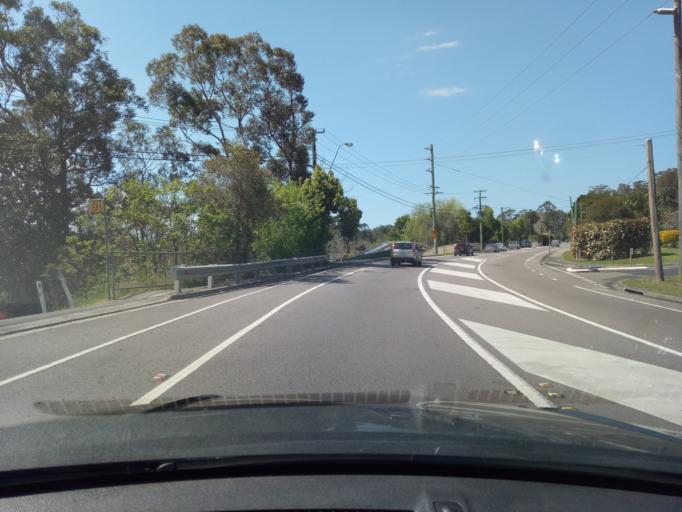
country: AU
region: New South Wales
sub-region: Gosford Shire
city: Narara
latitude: -33.4052
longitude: 151.3375
